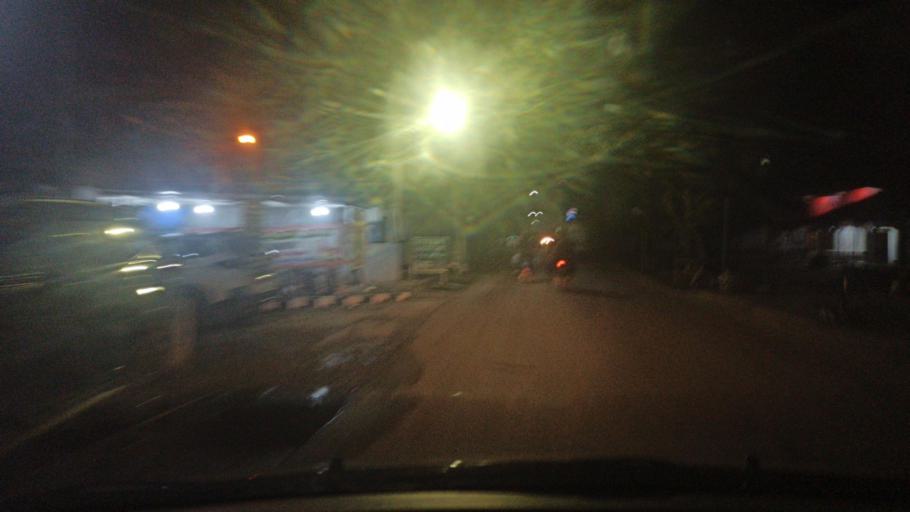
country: ID
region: South Sumatra
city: Palembang
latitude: -2.9237
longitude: 104.7840
